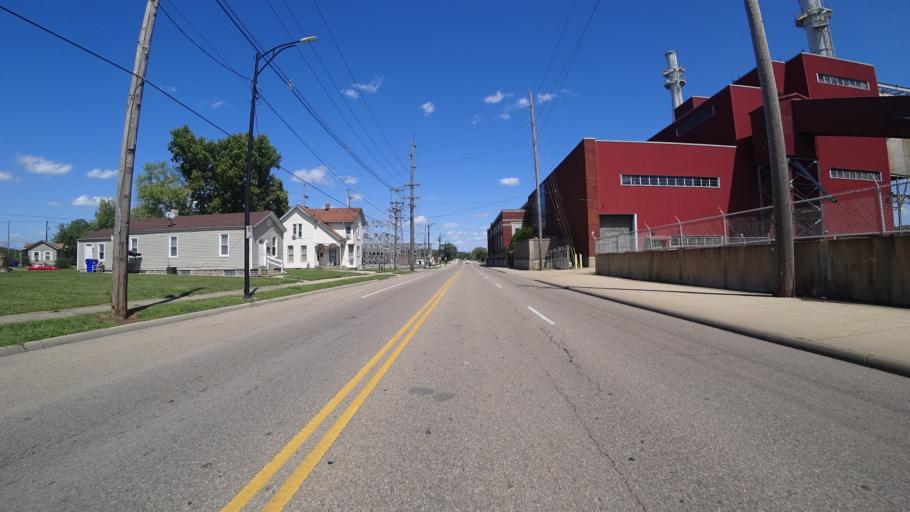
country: US
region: Ohio
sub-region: Butler County
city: Hamilton
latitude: 39.4095
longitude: -84.5553
